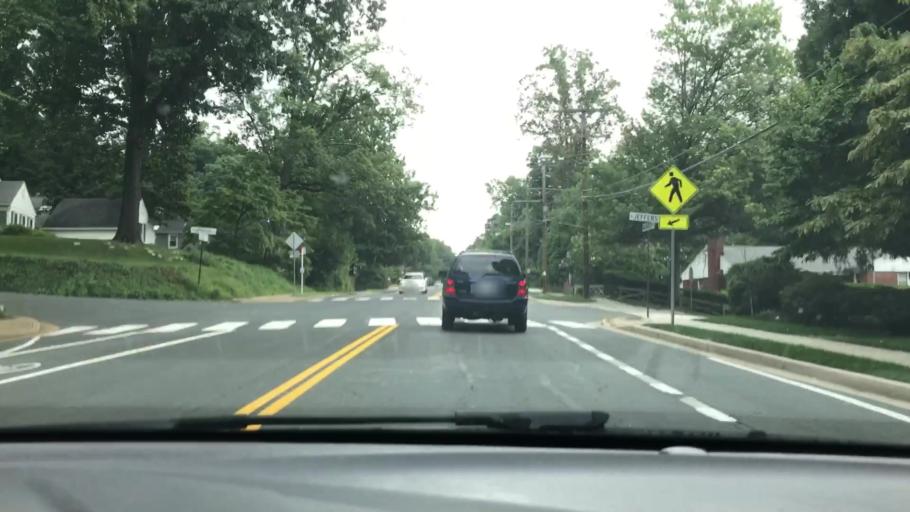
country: US
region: Virginia
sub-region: Fairfax County
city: Seven Corners
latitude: 38.8836
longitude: -77.1341
